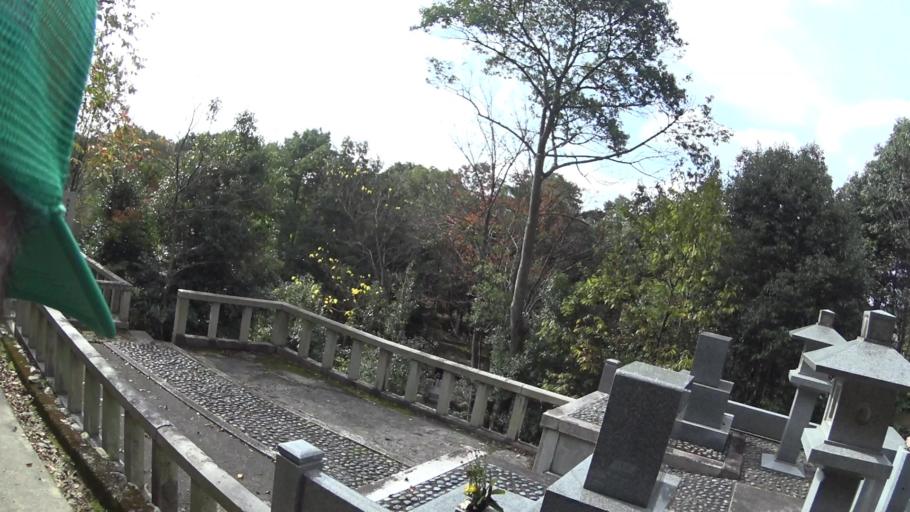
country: JP
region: Kyoto
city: Kyoto
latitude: 35.0324
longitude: 135.7158
